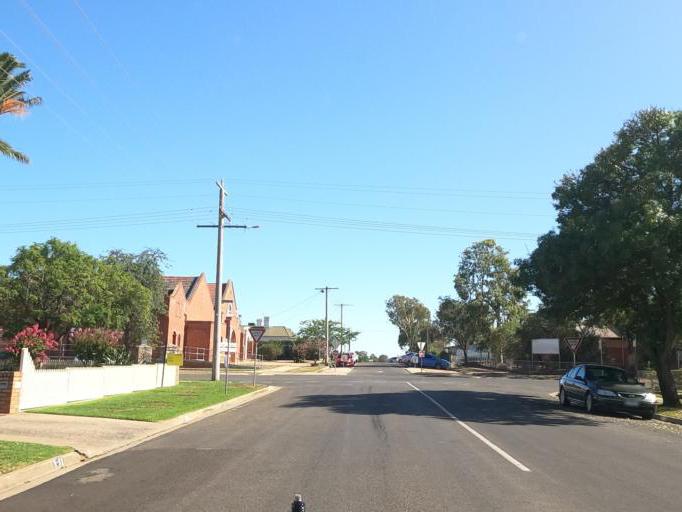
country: AU
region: Victoria
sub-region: Moira
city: Yarrawonga
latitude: -36.0114
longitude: 146.0017
